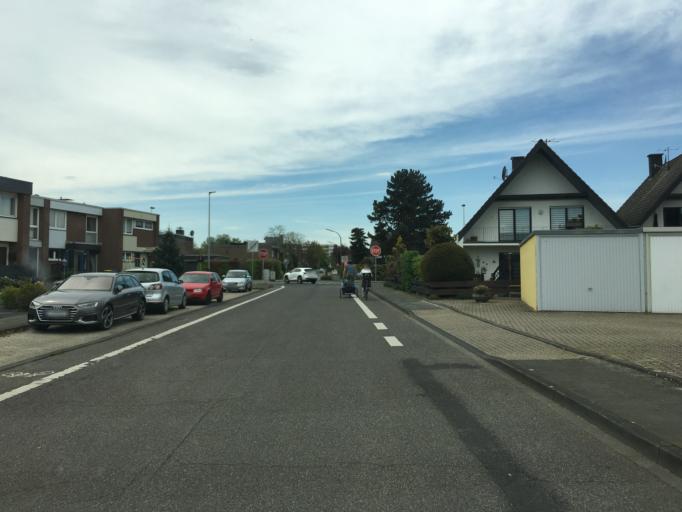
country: DE
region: North Rhine-Westphalia
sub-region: Regierungsbezirk Koln
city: Erftstadt
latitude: 50.8049
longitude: 6.7779
